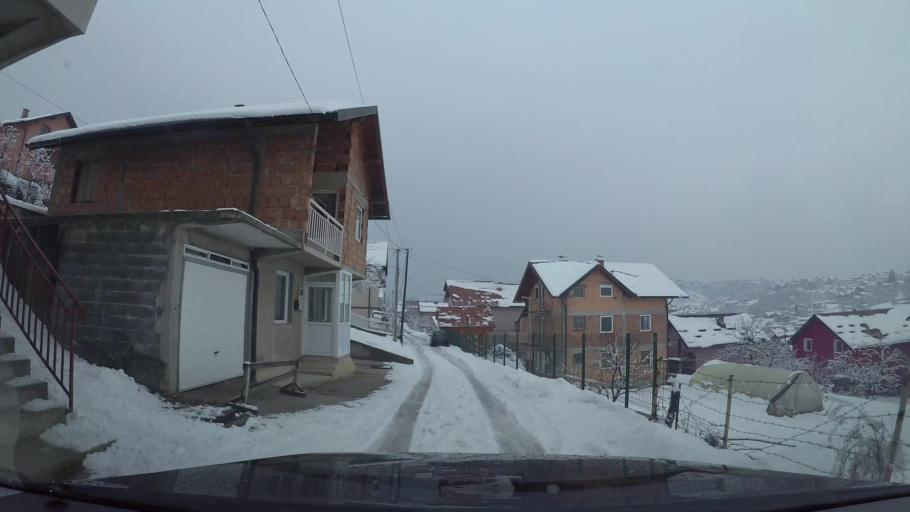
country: BA
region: Federation of Bosnia and Herzegovina
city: Vogosca
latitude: 43.8768
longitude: 18.3198
